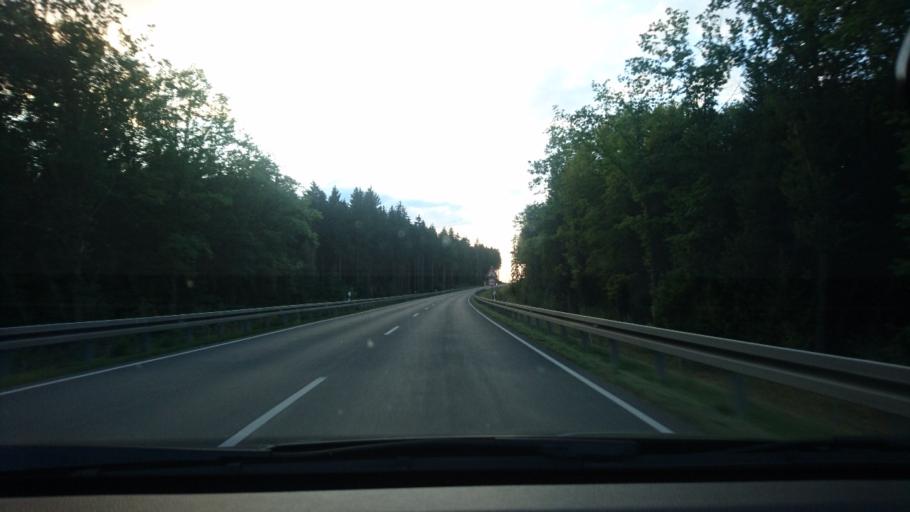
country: DE
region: Saxony
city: Lengenfeld
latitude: 50.5374
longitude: 12.3693
